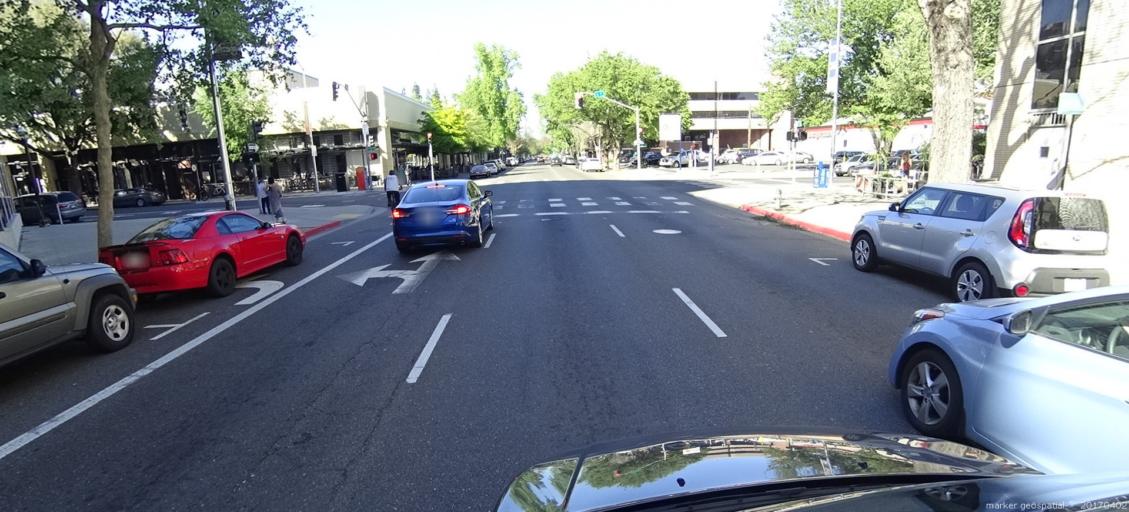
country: US
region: California
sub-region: Sacramento County
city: Sacramento
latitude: 38.5755
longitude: -121.4864
